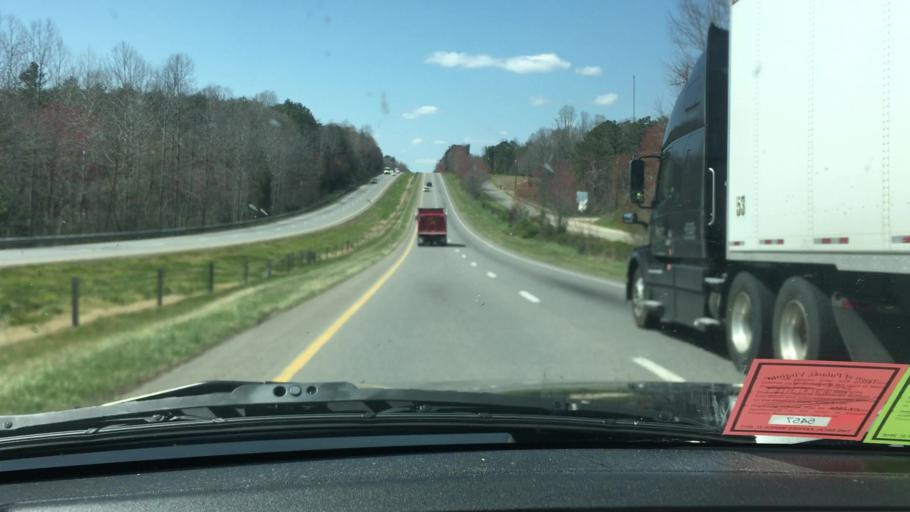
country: US
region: North Carolina
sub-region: Surry County
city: Pilot Mountain
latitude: 36.4248
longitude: -80.5191
